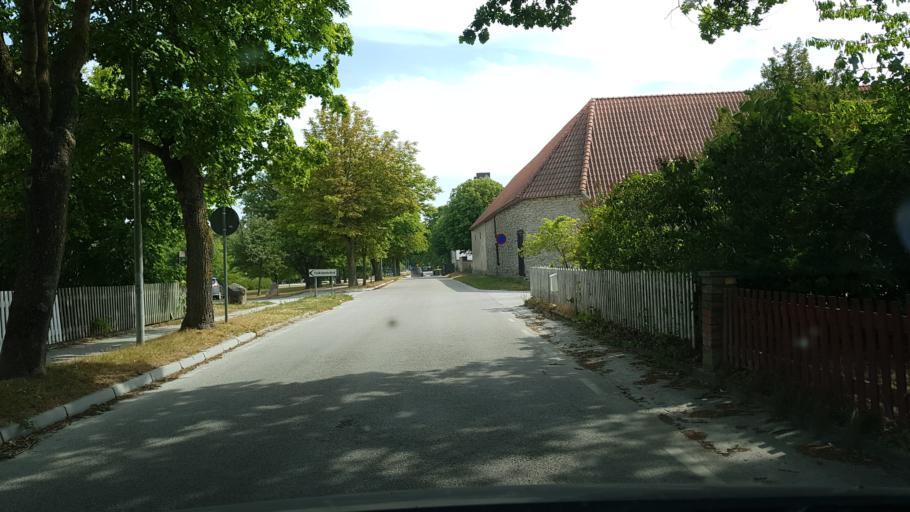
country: SE
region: Gotland
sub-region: Gotland
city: Slite
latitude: 57.7072
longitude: 18.8034
